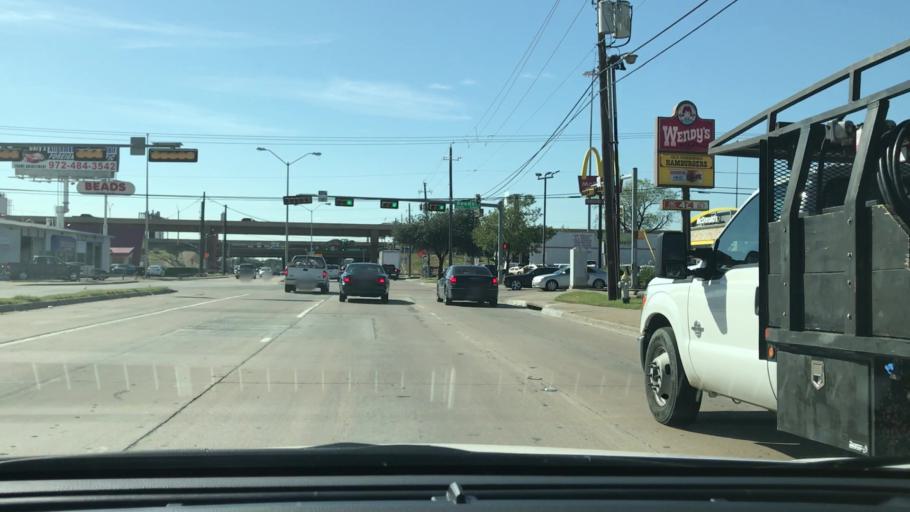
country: US
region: Texas
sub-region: Dallas County
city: Farmers Branch
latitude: 32.8961
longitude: -96.8956
